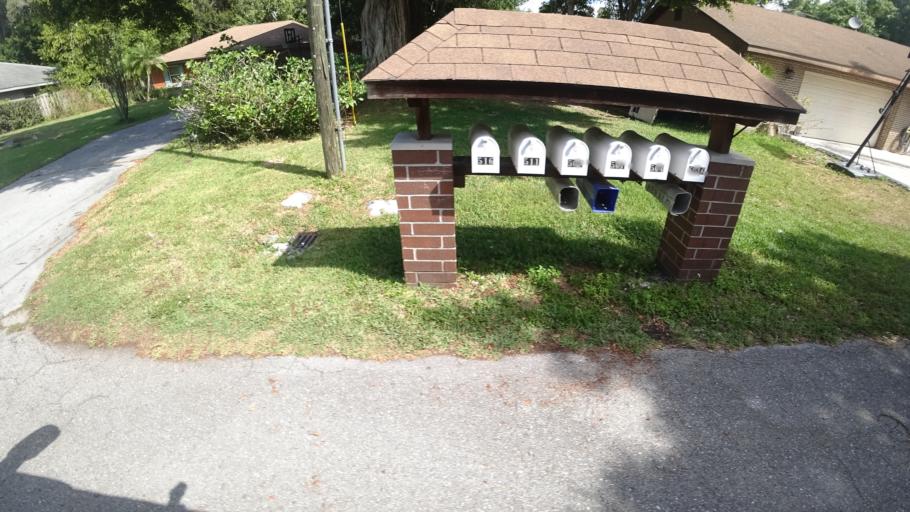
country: US
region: Florida
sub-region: Manatee County
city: Whitfield
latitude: 27.4194
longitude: -82.5677
